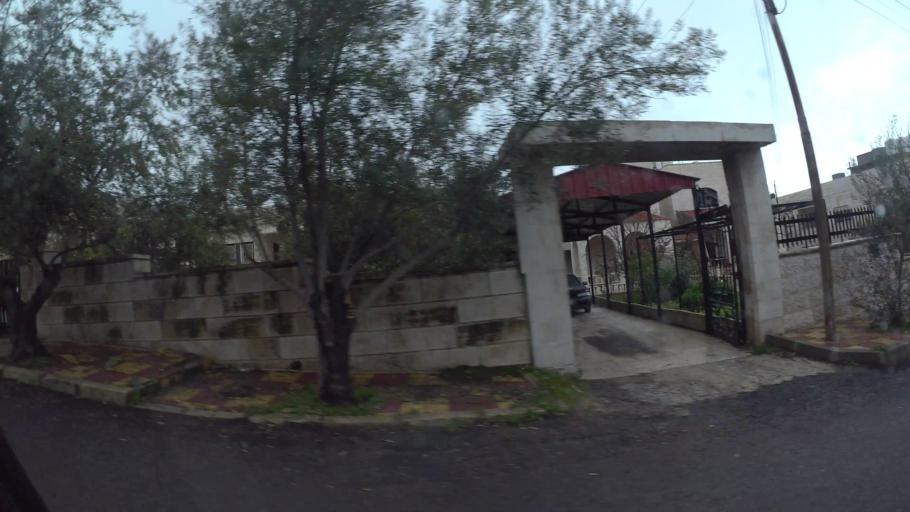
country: JO
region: Amman
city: Al Jubayhah
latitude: 32.0342
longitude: 35.8357
